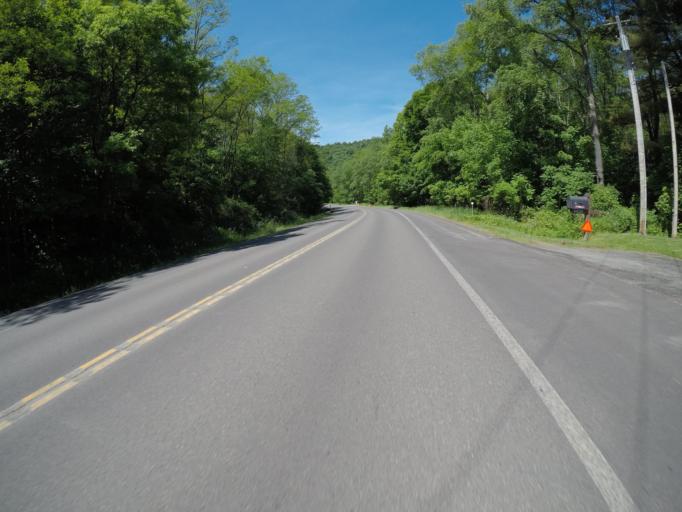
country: US
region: New York
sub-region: Delaware County
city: Walton
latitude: 42.1683
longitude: -75.0388
